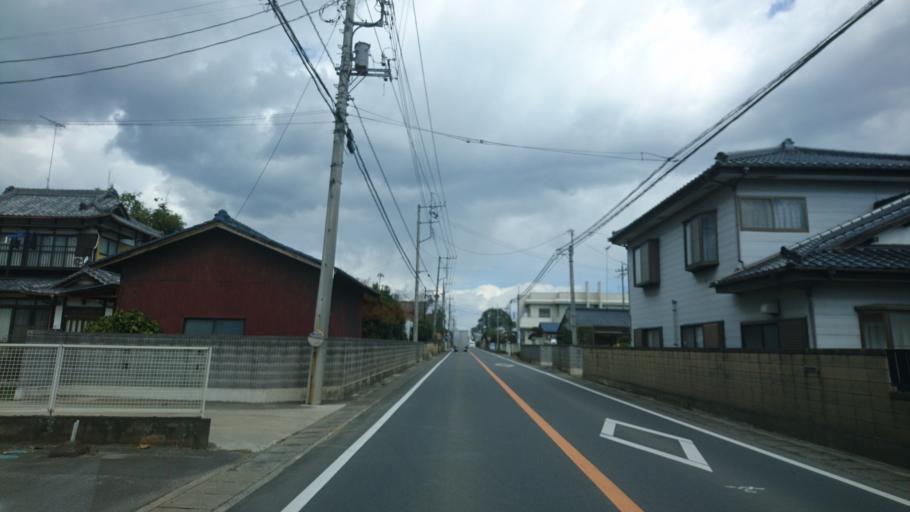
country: JP
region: Ibaraki
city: Yuki
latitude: 36.2303
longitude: 139.9320
